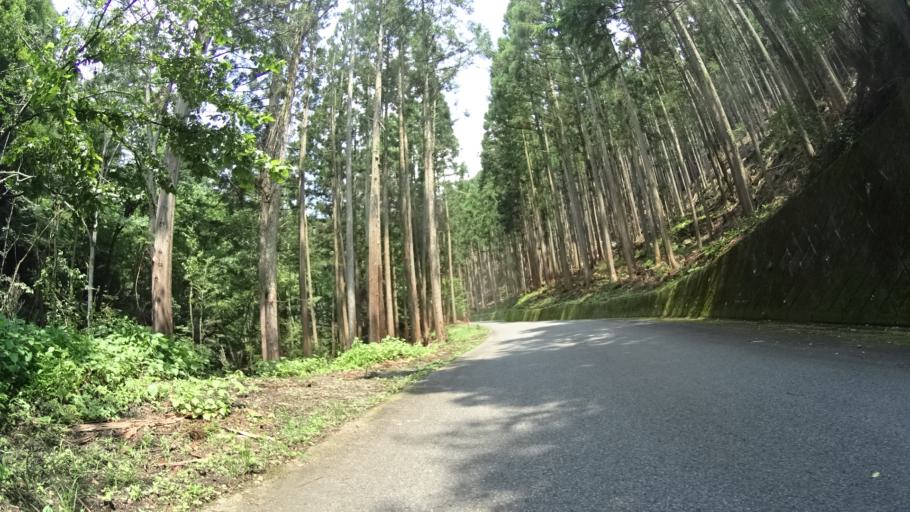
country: JP
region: Gunma
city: Tomioka
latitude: 36.0865
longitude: 138.7064
